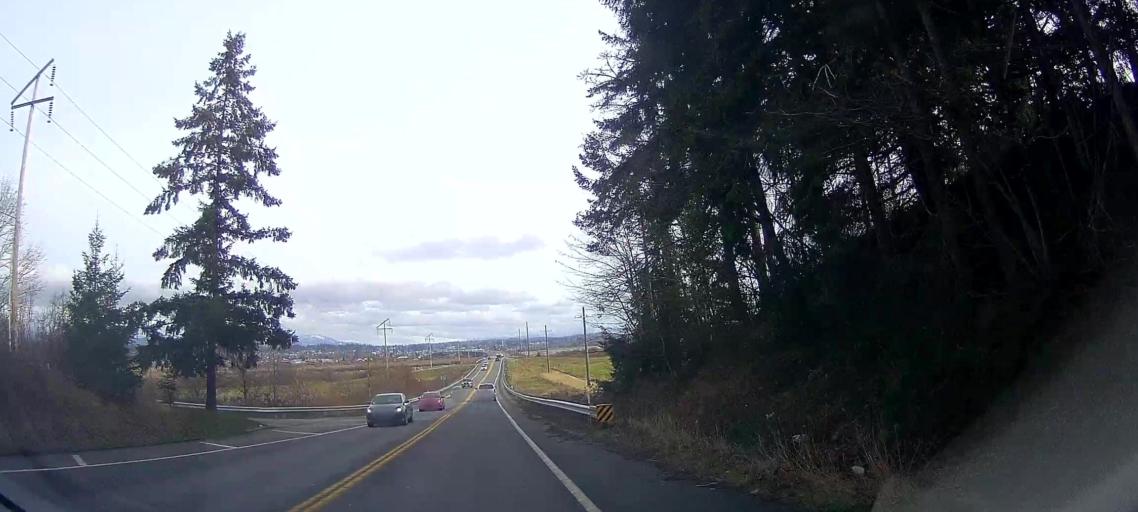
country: US
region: Washington
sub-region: Snohomish County
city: Stanwood
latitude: 48.2401
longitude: -122.4023
